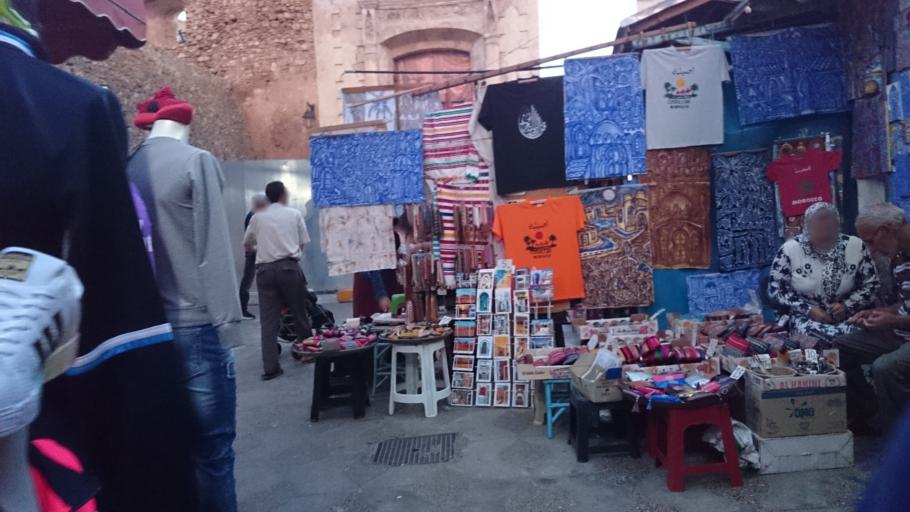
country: MA
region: Tanger-Tetouan
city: Asilah
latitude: 35.4656
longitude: -6.0375
